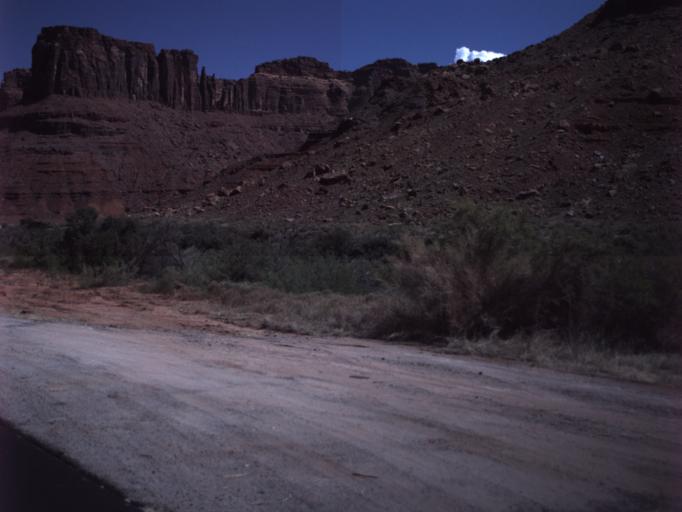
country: US
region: Utah
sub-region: Grand County
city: Moab
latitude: 38.6470
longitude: -109.4937
